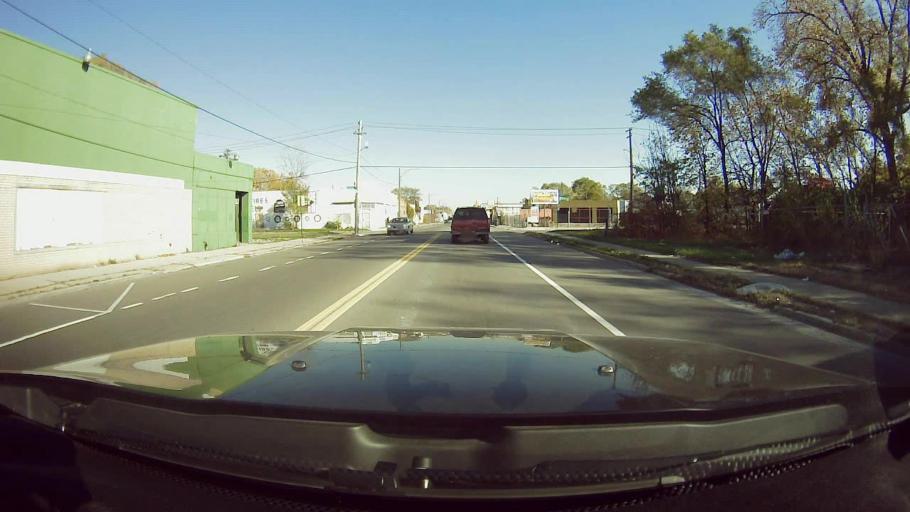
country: US
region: Michigan
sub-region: Wayne County
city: Highland Park
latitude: 42.4325
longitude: -83.0935
